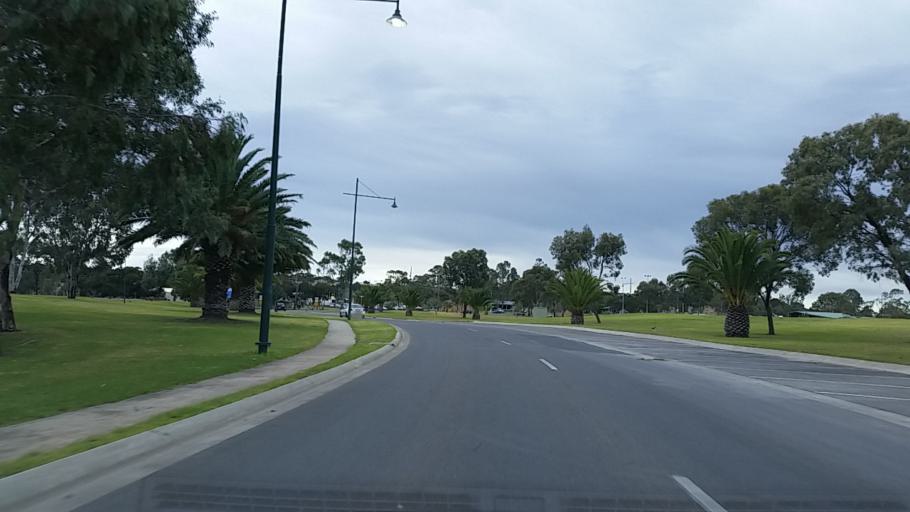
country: AU
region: South Australia
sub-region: Murray Bridge
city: Murray Bridge
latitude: -35.1213
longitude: 139.2803
